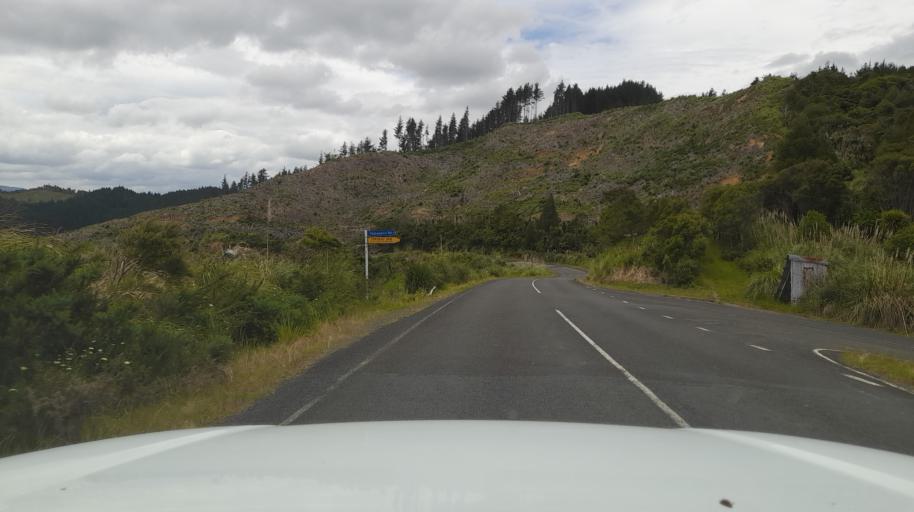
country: NZ
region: Northland
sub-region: Far North District
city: Kaitaia
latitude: -35.3720
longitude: 173.4304
